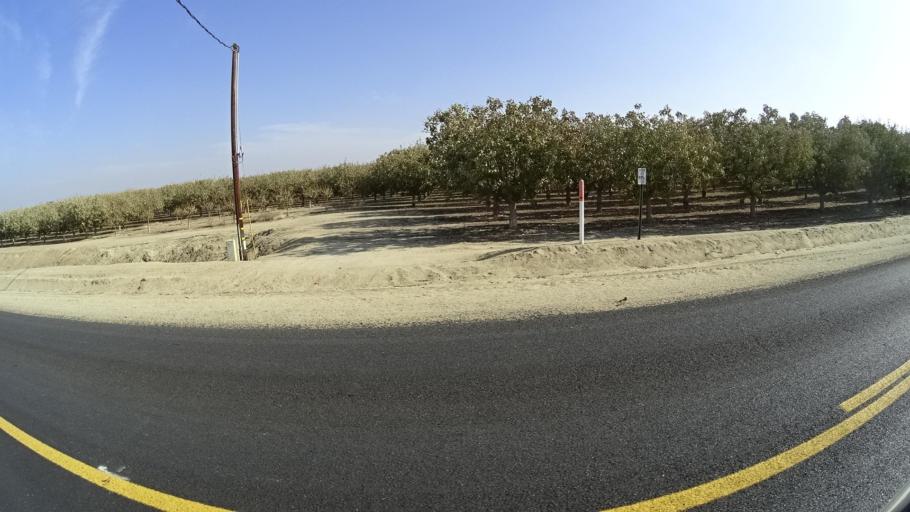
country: US
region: California
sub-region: Kern County
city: Shafter
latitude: 35.5500
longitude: -119.1513
